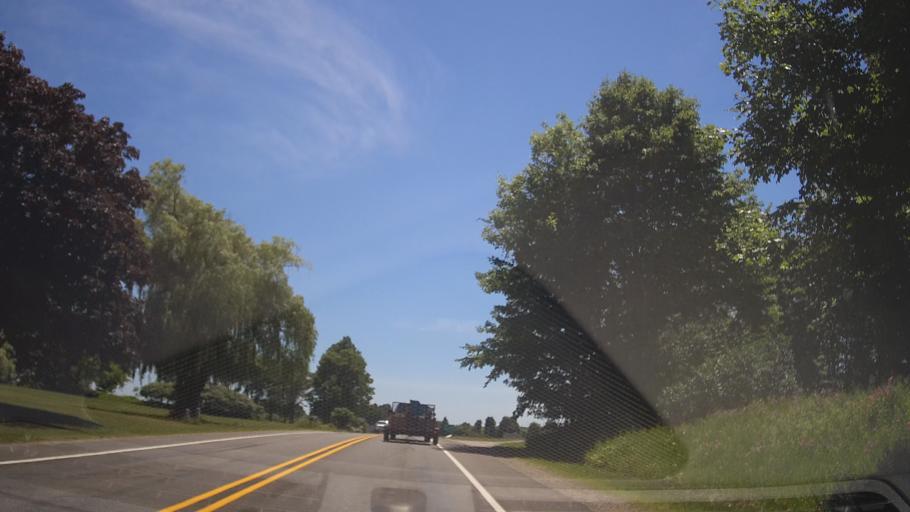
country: US
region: Michigan
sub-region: Grand Traverse County
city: Traverse City
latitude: 44.6183
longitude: -85.6966
